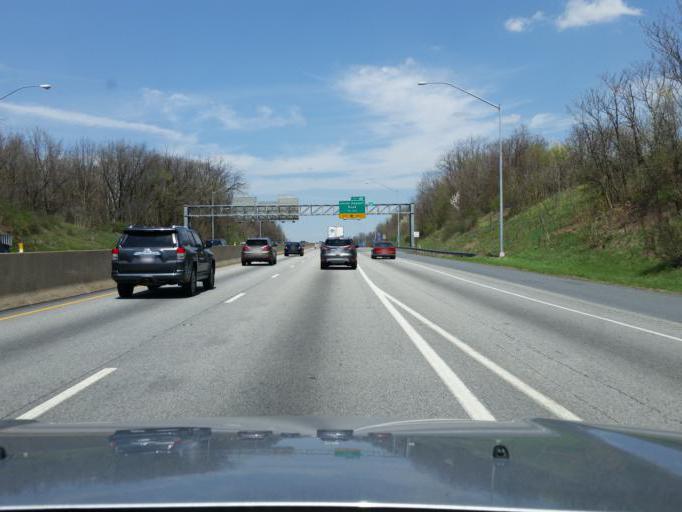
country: US
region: Pennsylvania
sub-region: Dauphin County
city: Lawnton
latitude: 40.2623
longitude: -76.8143
